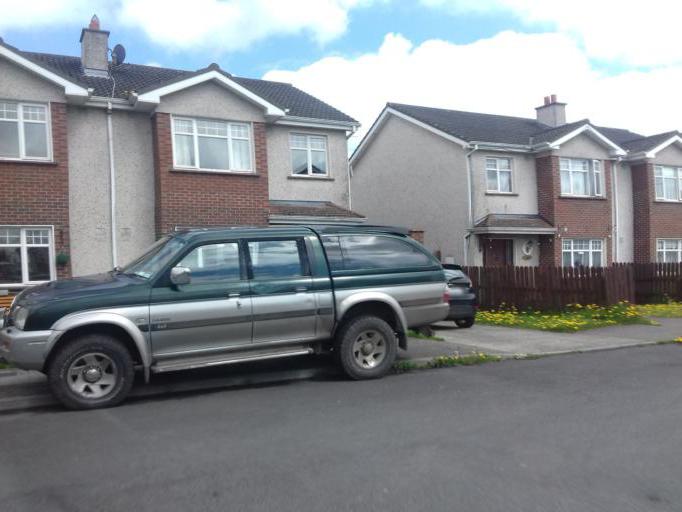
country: IE
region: Leinster
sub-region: Laois
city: Portlaoise
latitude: 53.0451
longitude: -7.3096
